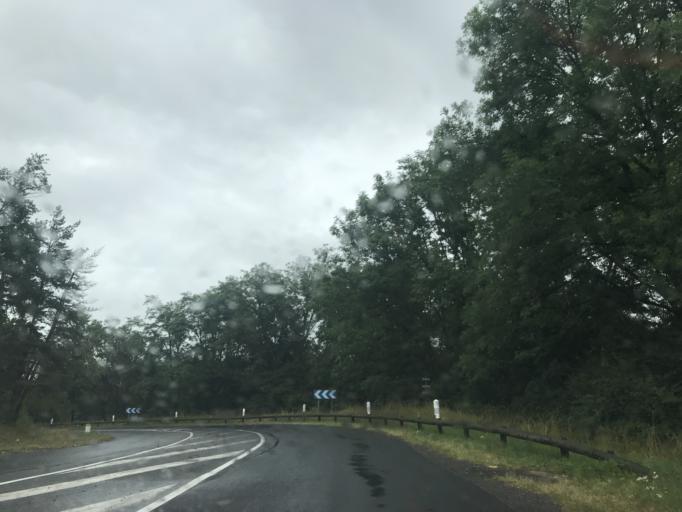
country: FR
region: Auvergne
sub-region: Departement du Puy-de-Dome
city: Ambert
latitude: 45.5478
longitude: 3.7296
